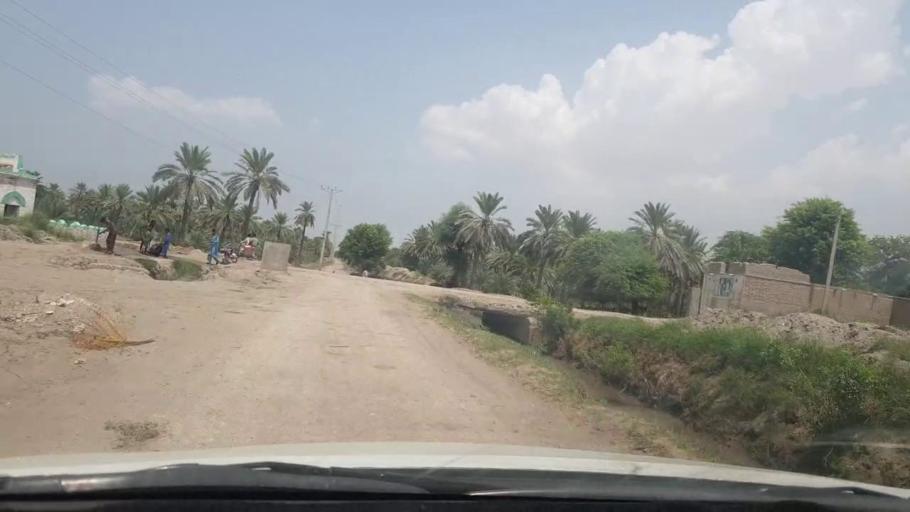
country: PK
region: Sindh
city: Khairpur
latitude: 27.5517
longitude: 68.8537
